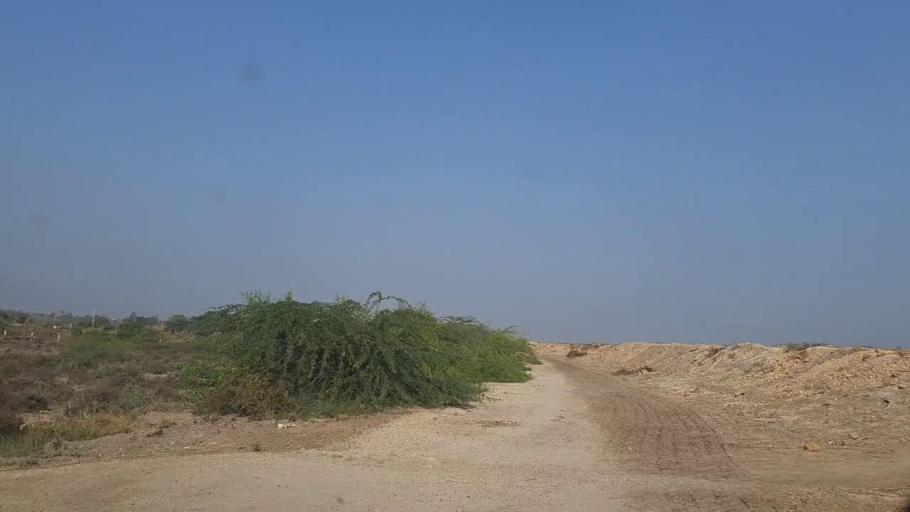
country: PK
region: Sindh
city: Thatta
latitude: 24.6573
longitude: 67.9270
